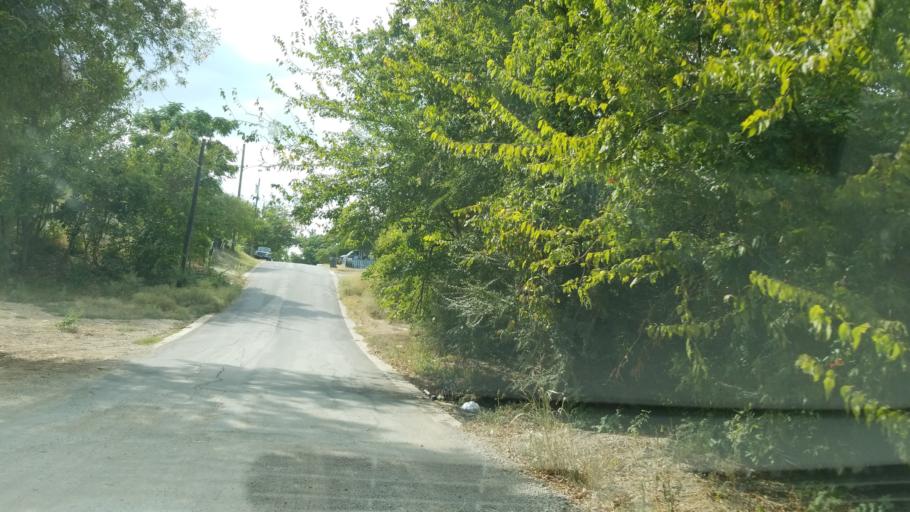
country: US
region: Texas
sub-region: Dallas County
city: Dallas
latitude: 32.7695
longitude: -96.8459
